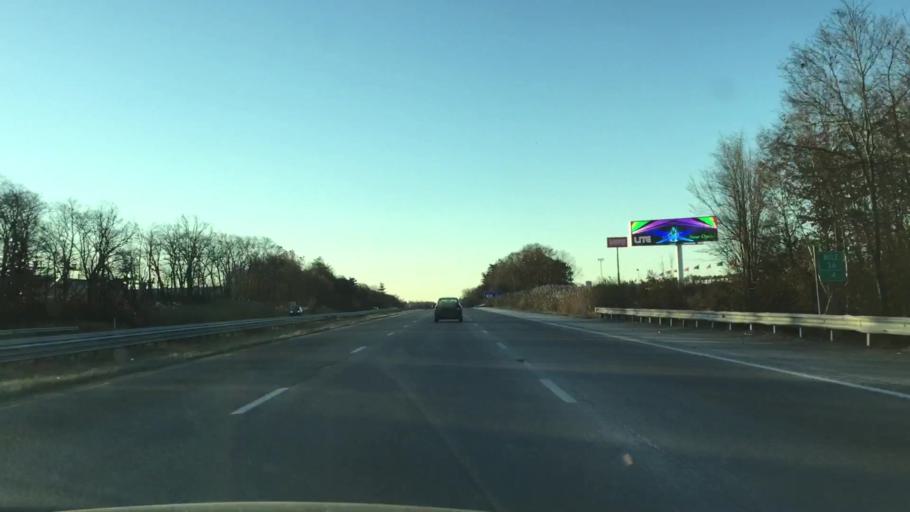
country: US
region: Massachusetts
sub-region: Norfolk County
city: Avon
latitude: 42.1361
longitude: -71.0647
